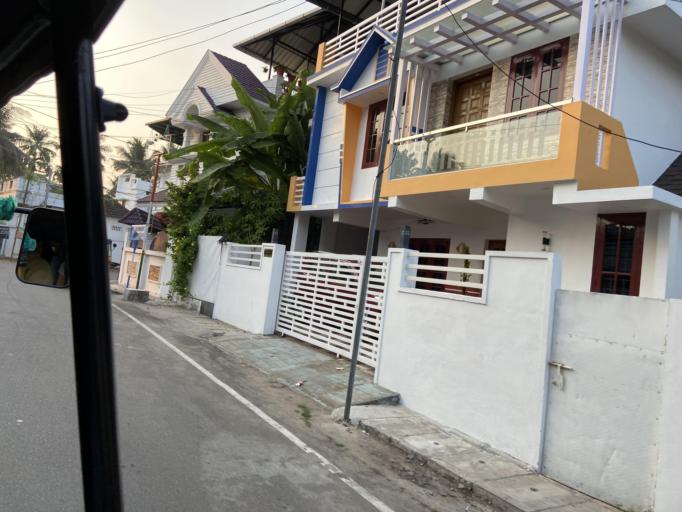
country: IN
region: Kerala
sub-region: Ernakulam
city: Cochin
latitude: 9.9443
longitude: 76.2459
